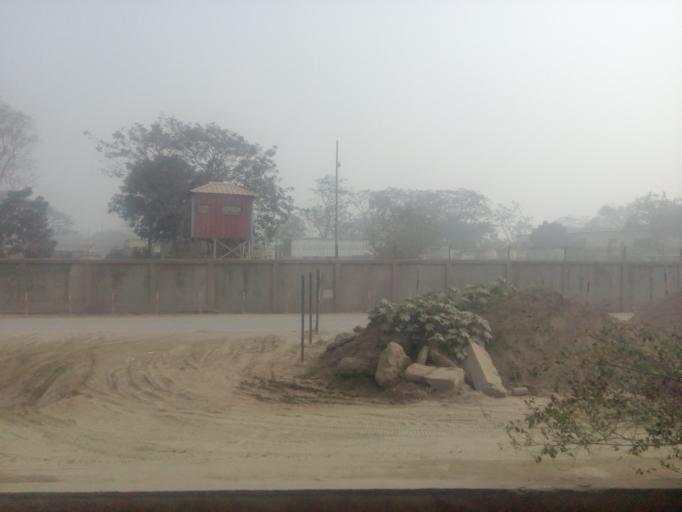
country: BD
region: Dhaka
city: Narayanganj
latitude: 23.6123
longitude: 90.6112
